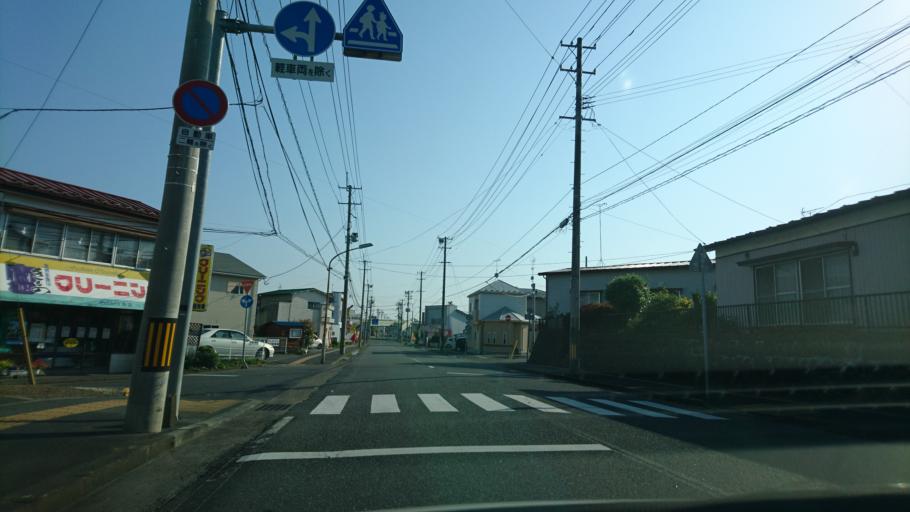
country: JP
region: Iwate
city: Ichinoseki
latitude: 38.9326
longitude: 141.1240
